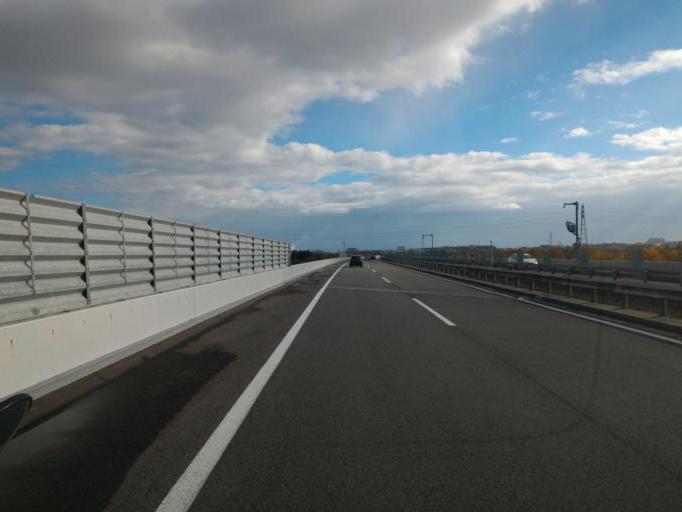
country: JP
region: Hokkaido
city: Ebetsu
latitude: 43.0933
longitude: 141.4703
